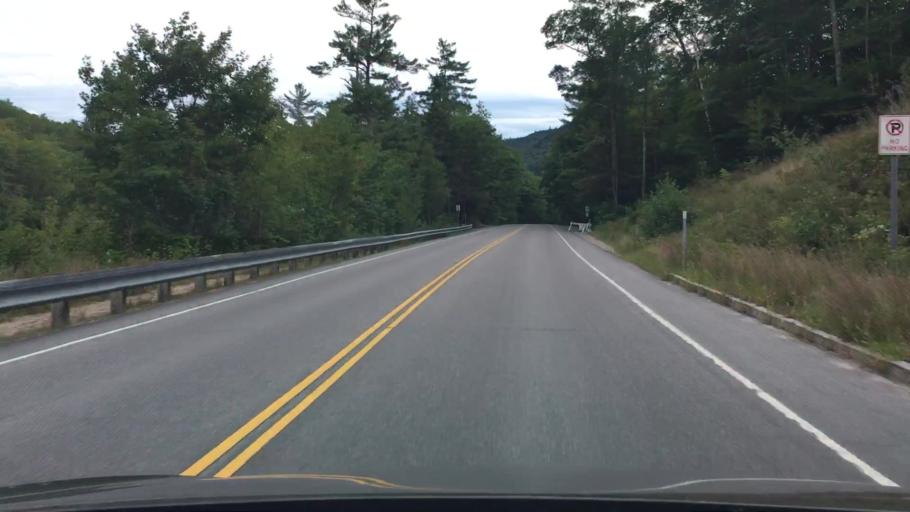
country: US
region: New Hampshire
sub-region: Carroll County
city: North Conway
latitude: 44.0138
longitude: -71.2449
